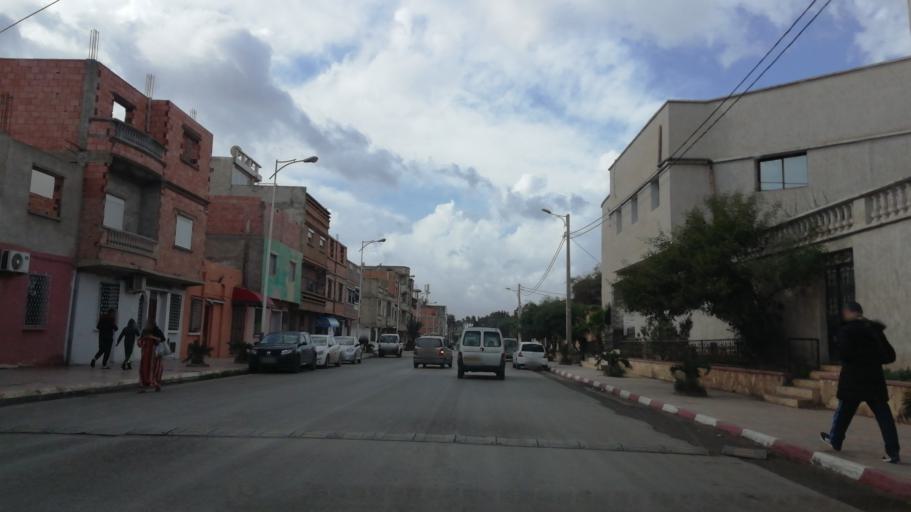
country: DZ
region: Oran
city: Oran
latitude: 35.6800
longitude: -0.6186
